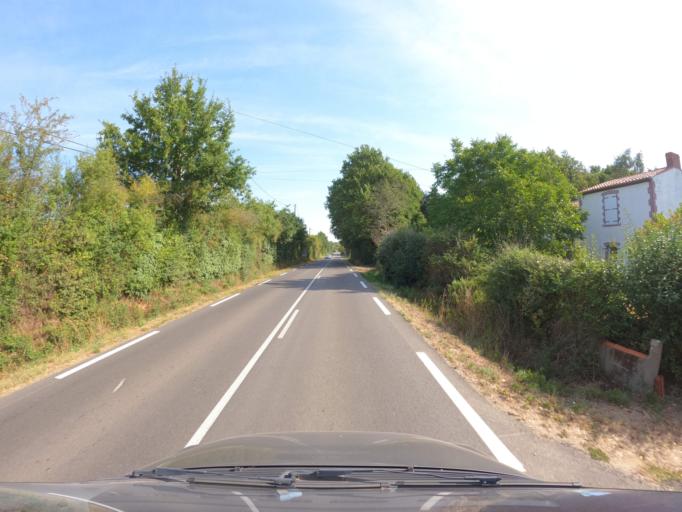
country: FR
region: Pays de la Loire
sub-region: Departement de la Vendee
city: Saint-Christophe-du-Ligneron
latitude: 46.8086
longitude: -1.7755
